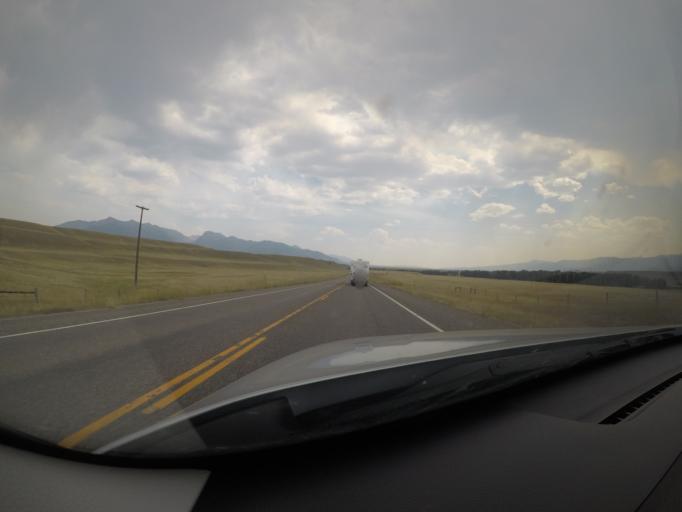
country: US
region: Montana
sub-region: Gallatin County
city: Big Sky
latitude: 45.1128
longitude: -111.6569
